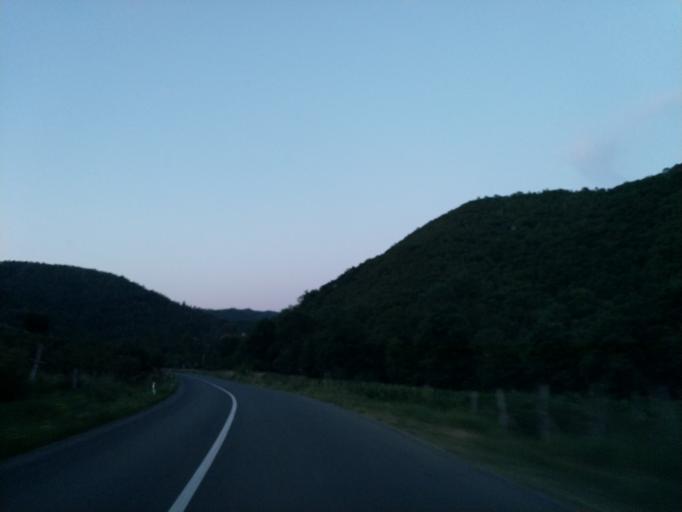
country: RS
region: Central Serbia
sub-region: Rasinski Okrug
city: Aleksandrovac
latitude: 43.3430
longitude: 21.0985
